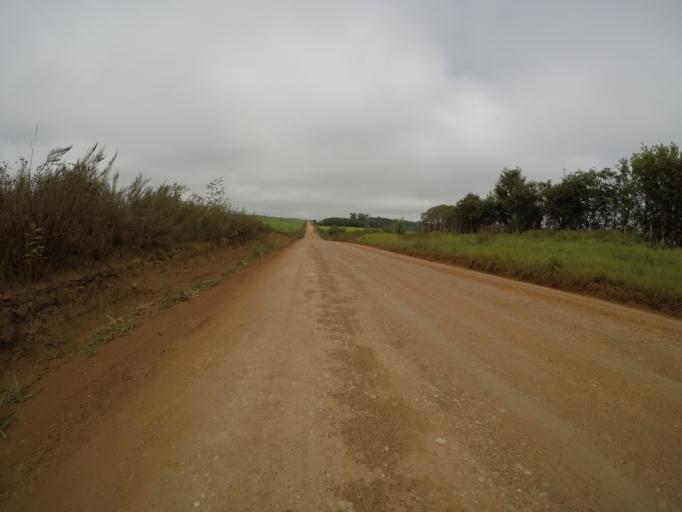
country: ZA
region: Eastern Cape
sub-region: Cacadu District Municipality
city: Kareedouw
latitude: -34.0104
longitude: 24.2367
